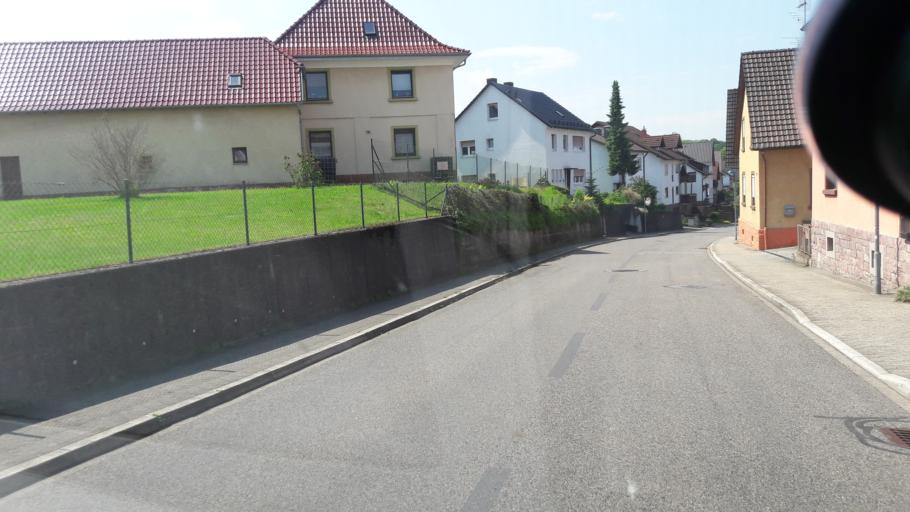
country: DE
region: Baden-Wuerttemberg
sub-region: Karlsruhe Region
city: Malsch
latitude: 48.8796
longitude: 8.3315
